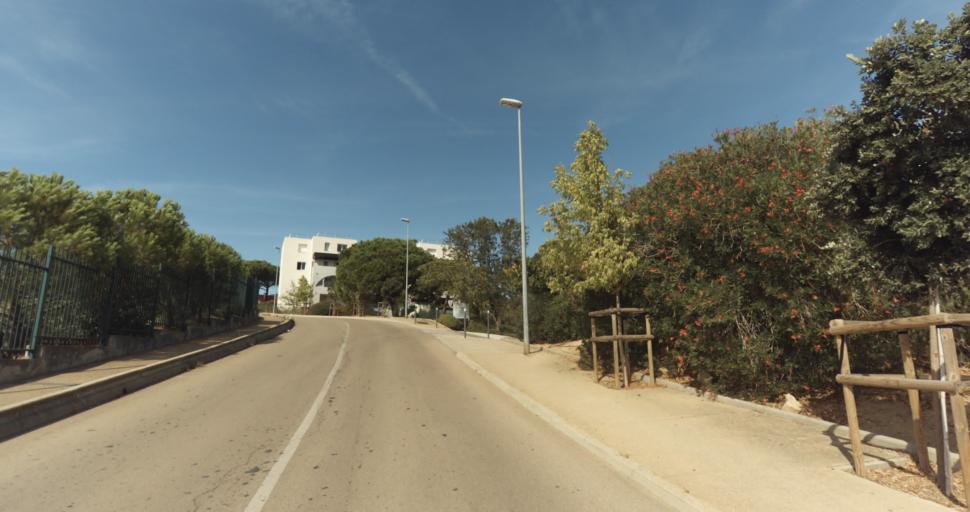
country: FR
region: Corsica
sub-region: Departement de la Corse-du-Sud
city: Ajaccio
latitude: 41.9428
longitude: 8.7471
